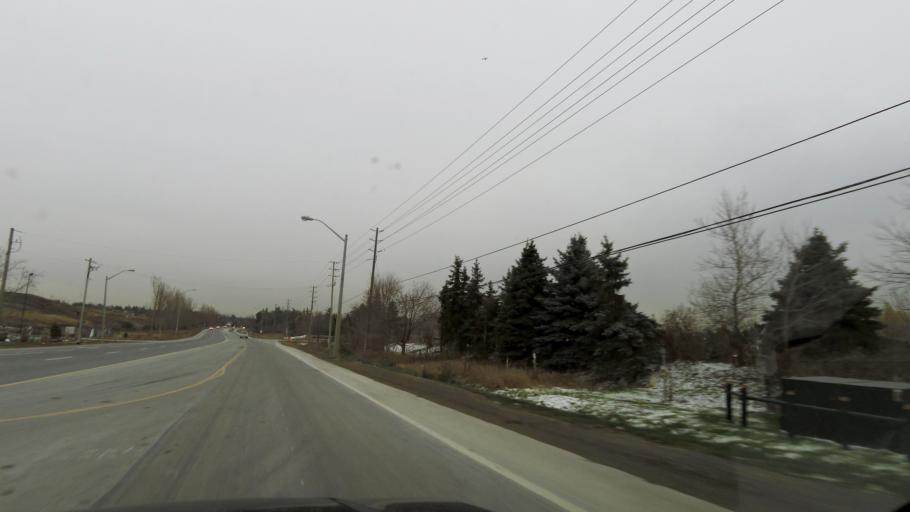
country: CA
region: Ontario
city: Vaughan
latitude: 43.8523
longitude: -79.6397
